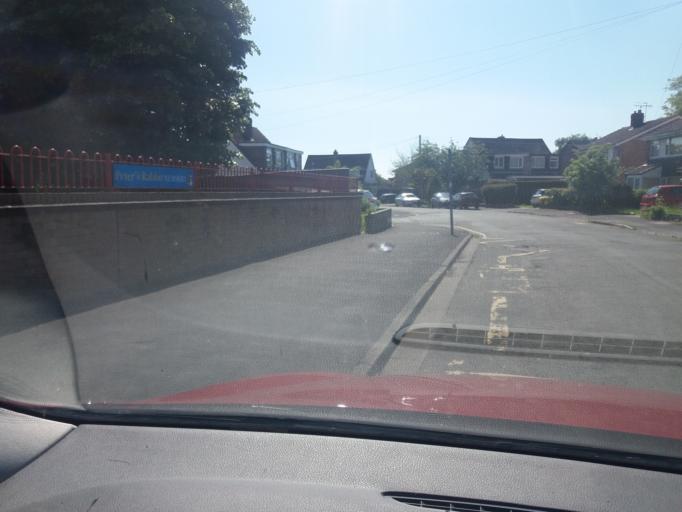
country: GB
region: England
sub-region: Lancashire
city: Preston
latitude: 53.7961
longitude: -2.7049
